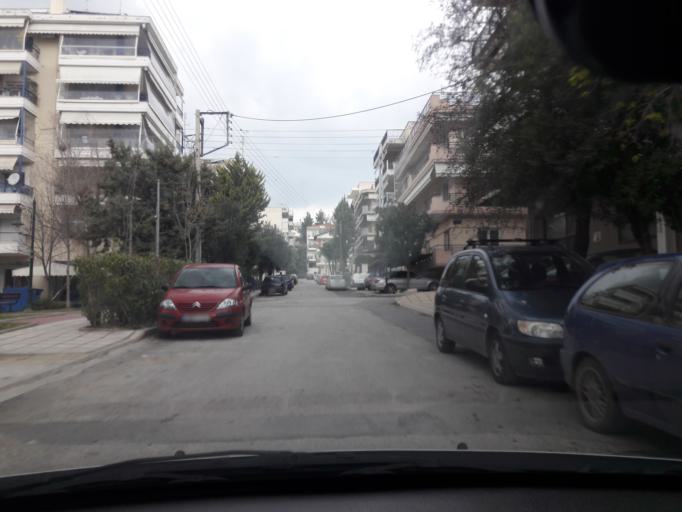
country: GR
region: Central Macedonia
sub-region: Nomos Thessalonikis
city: Evosmos
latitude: 40.6683
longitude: 22.9231
